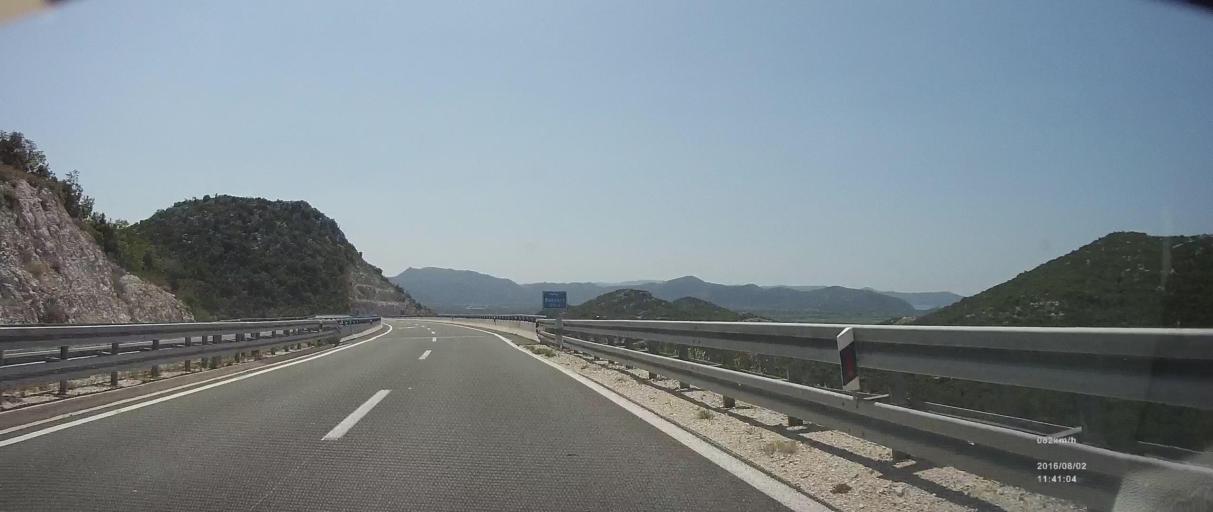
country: HR
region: Dubrovacko-Neretvanska
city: Komin
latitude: 43.0676
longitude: 17.4936
